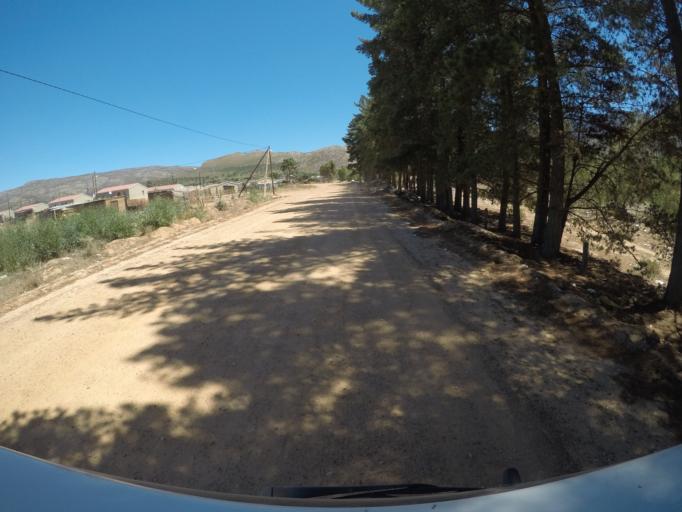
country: ZA
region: Western Cape
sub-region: Overberg District Municipality
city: Grabouw
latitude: -34.2219
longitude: 19.1967
